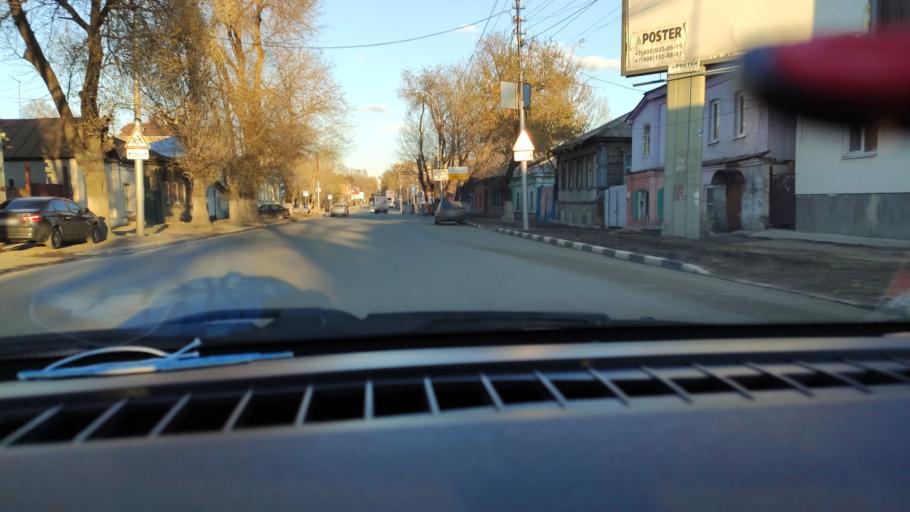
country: RU
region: Saratov
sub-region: Saratovskiy Rayon
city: Saratov
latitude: 51.5399
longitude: 46.0410
